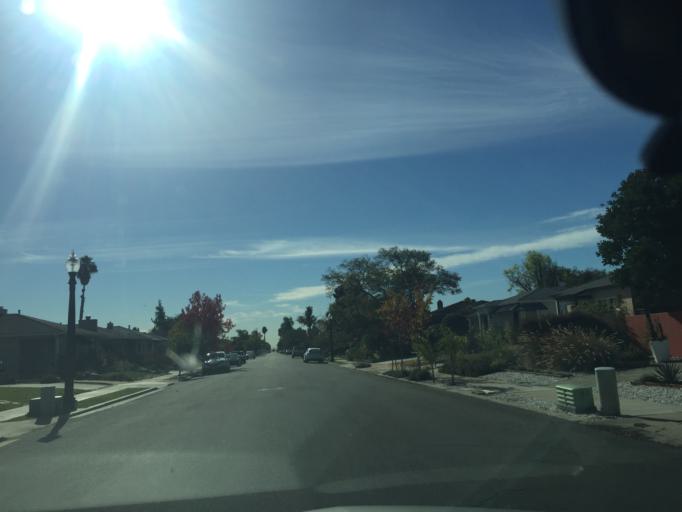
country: US
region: California
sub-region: San Diego County
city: Lemon Grove
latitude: 32.7642
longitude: -117.0867
